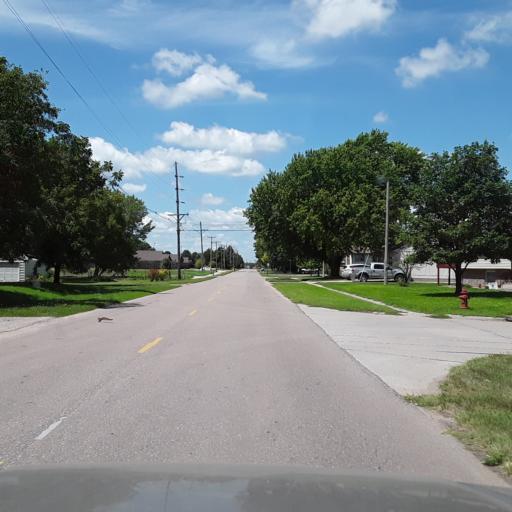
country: US
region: Nebraska
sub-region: Merrick County
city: Central City
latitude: 41.1048
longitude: -98.0090
